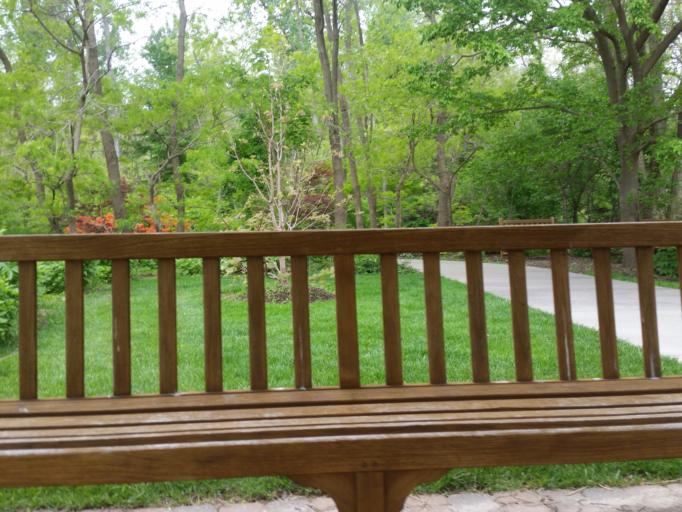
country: US
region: Nebraska
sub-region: Douglas County
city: Omaha
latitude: 41.2386
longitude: -95.9176
